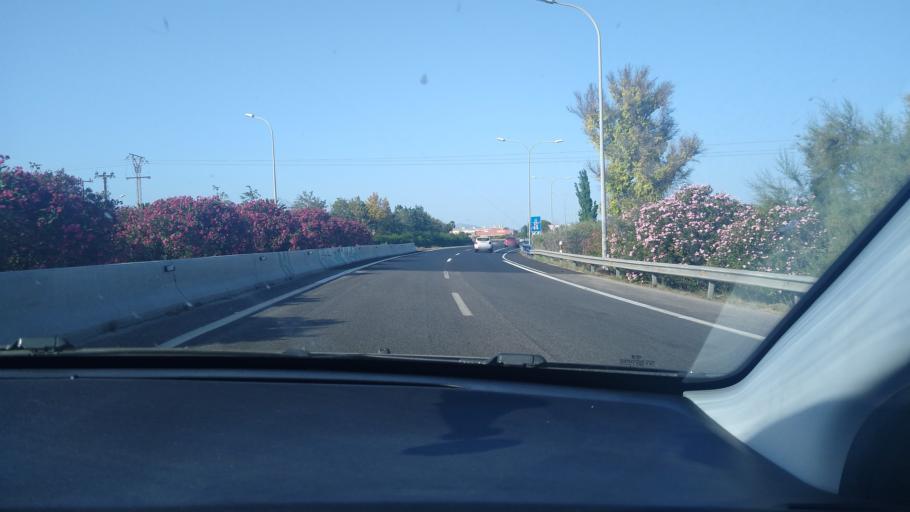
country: ES
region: Balearic Islands
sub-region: Illes Balears
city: Palma
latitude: 39.5875
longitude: 2.6690
